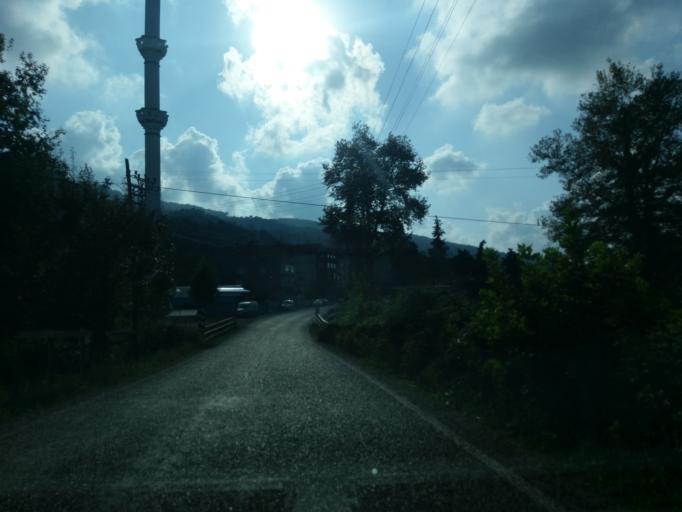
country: TR
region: Sinop
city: Helaldi
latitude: 41.8904
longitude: 34.4860
